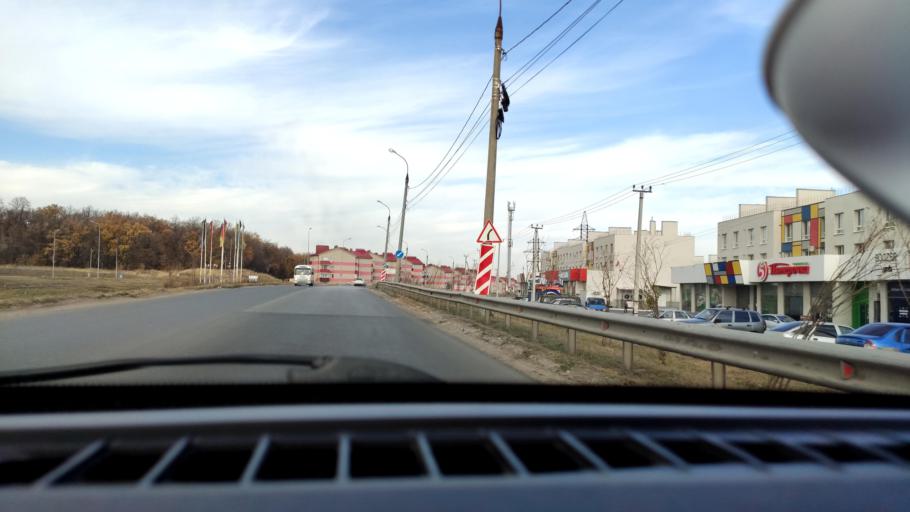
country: RU
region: Samara
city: Novosemeykino
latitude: 53.3263
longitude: 50.3108
